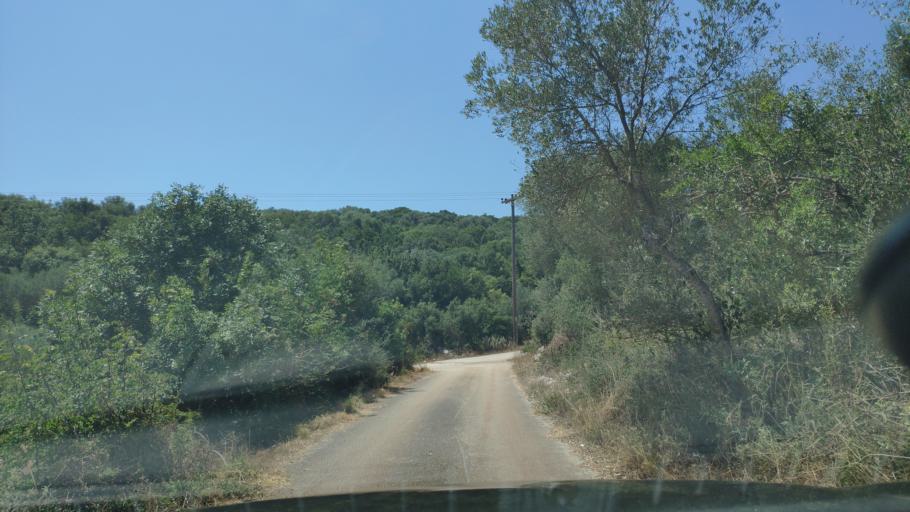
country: GR
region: West Greece
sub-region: Nomos Aitolias kai Akarnanias
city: Amfilochia
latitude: 38.9059
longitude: 21.1064
